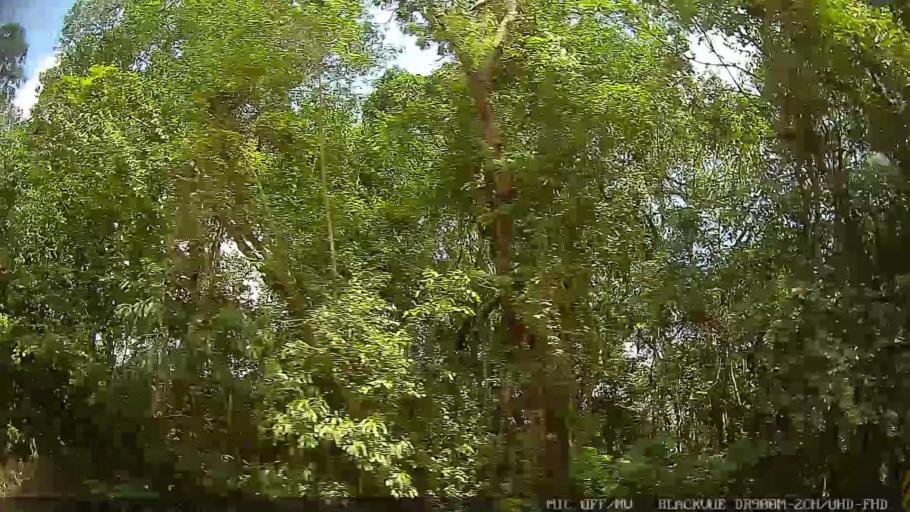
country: BR
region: Sao Paulo
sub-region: Itatiba
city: Itatiba
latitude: -22.9696
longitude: -46.7193
